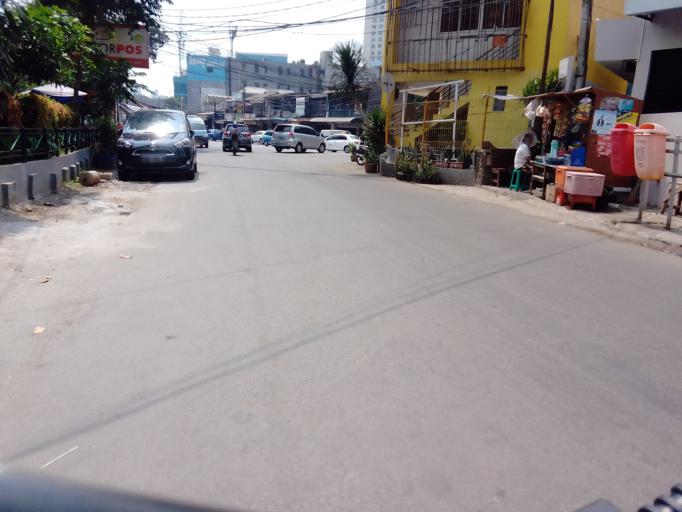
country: ID
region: Jakarta Raya
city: Jakarta
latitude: -6.2140
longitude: 106.8131
